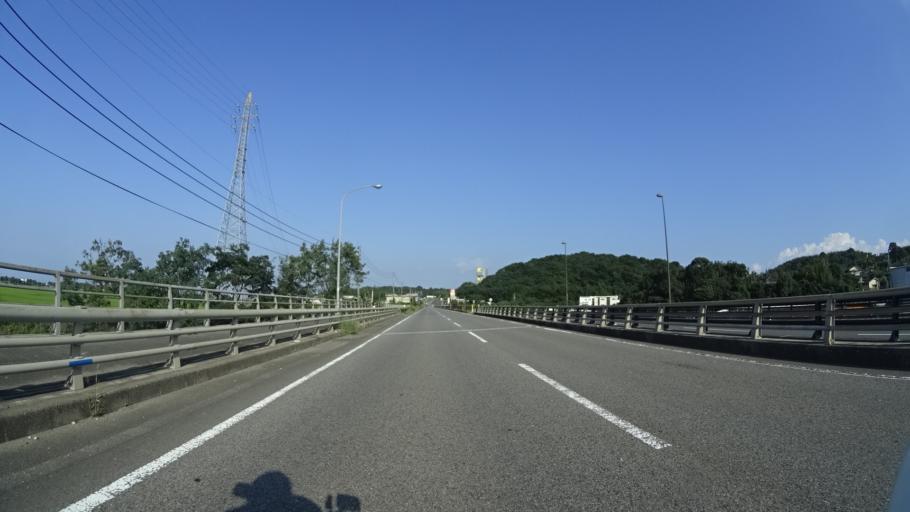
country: JP
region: Fukuoka
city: Nakatsu
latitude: 33.5524
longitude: 131.2166
